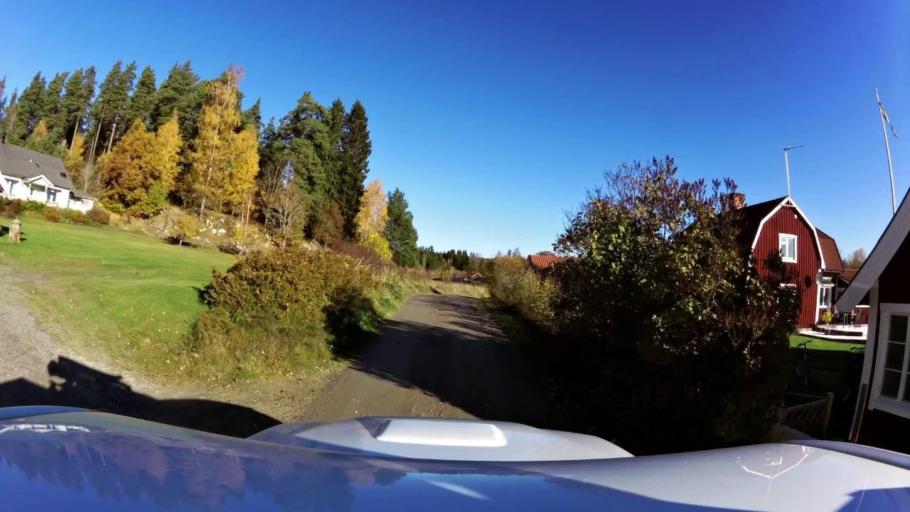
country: SE
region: OEstergoetland
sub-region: Linkopings Kommun
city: Ljungsbro
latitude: 58.5270
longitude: 15.4924
